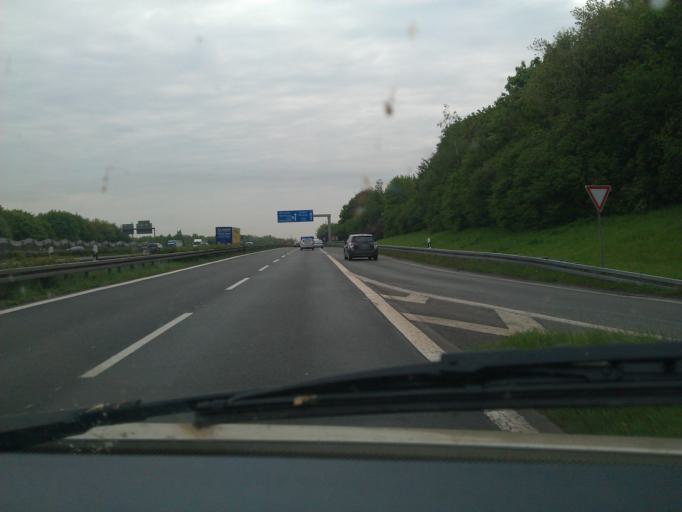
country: DE
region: North Rhine-Westphalia
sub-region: Regierungsbezirk Munster
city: Bottrop
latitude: 51.5485
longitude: 6.9137
